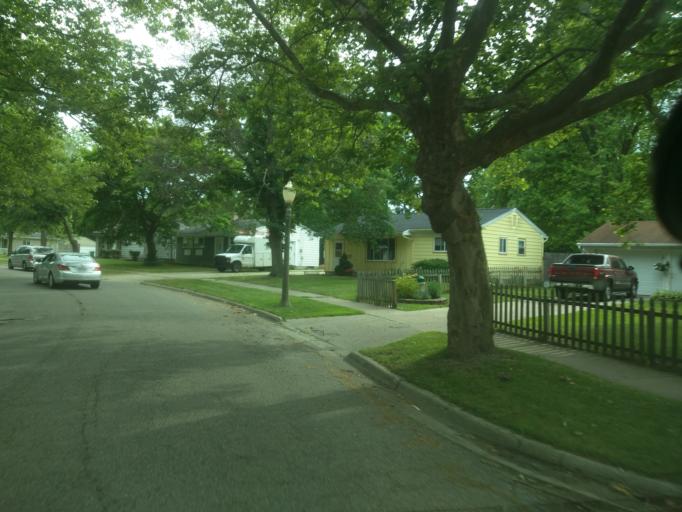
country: US
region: Michigan
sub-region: Eaton County
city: Waverly
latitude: 42.6954
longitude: -84.5963
